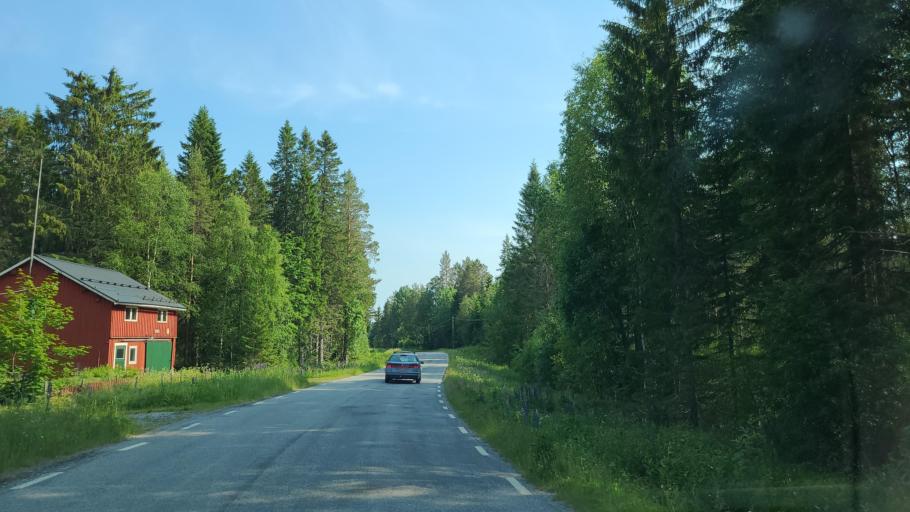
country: SE
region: Vaesterbotten
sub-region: Skelleftea Kommun
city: Burea
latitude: 64.3516
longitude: 21.3354
